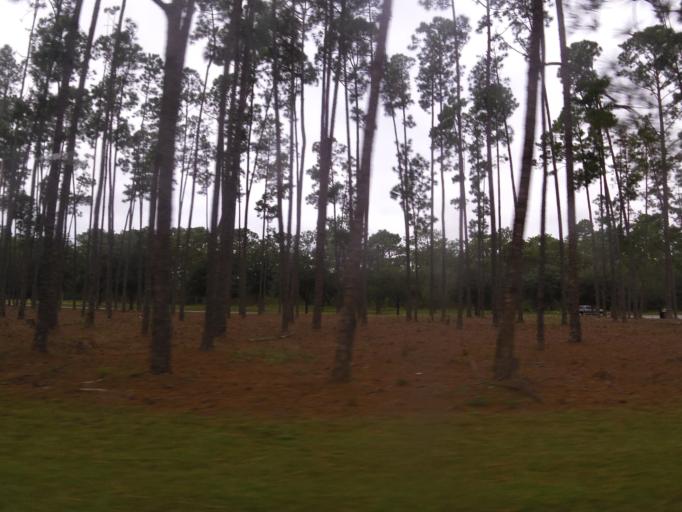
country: US
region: Florida
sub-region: Duval County
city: Baldwin
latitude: 30.2346
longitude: -81.8823
